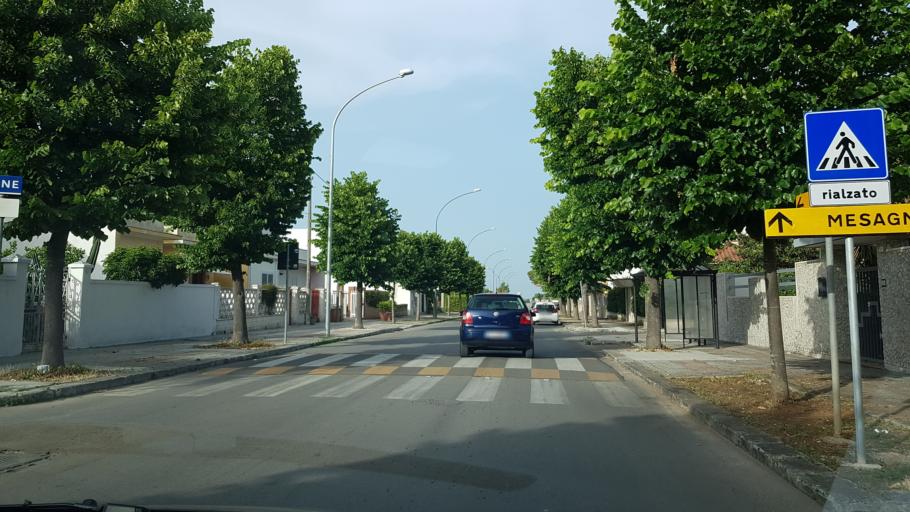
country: IT
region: Apulia
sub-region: Provincia di Brindisi
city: San Pancrazio Salentino
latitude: 40.4207
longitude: 17.8474
